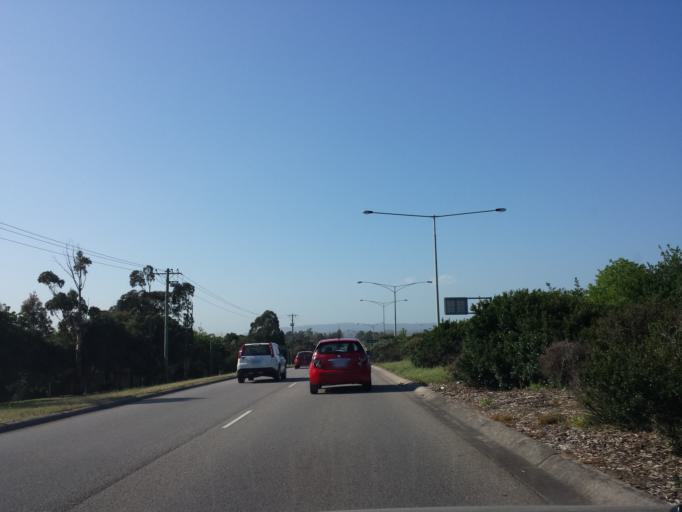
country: AU
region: Victoria
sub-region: Casey
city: Narre Warren
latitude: -38.0157
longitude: 145.3088
